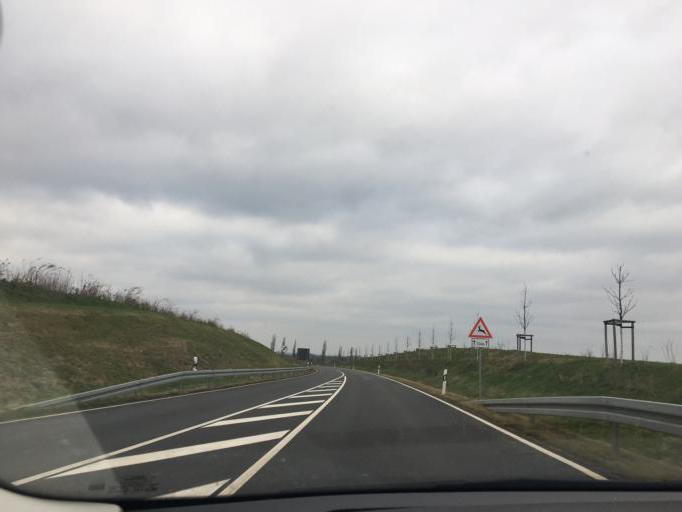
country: DE
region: Saxony
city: Niederfrohna
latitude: 50.8925
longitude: 12.7170
